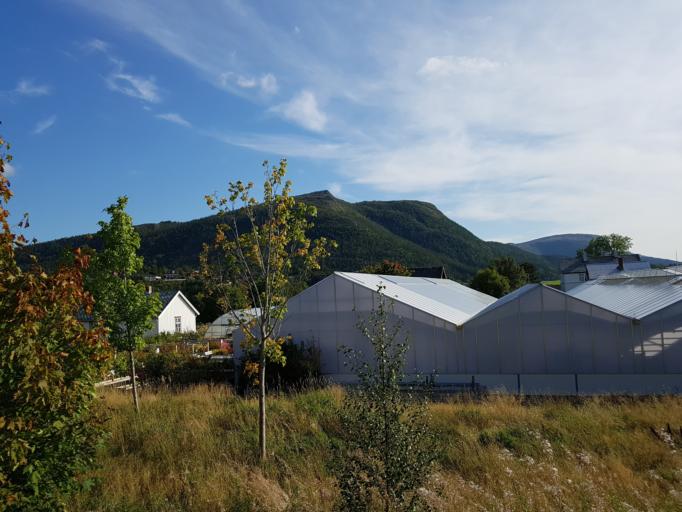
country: NO
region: Sor-Trondelag
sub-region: Afjord
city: A i Afjord
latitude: 63.9677
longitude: 10.2216
